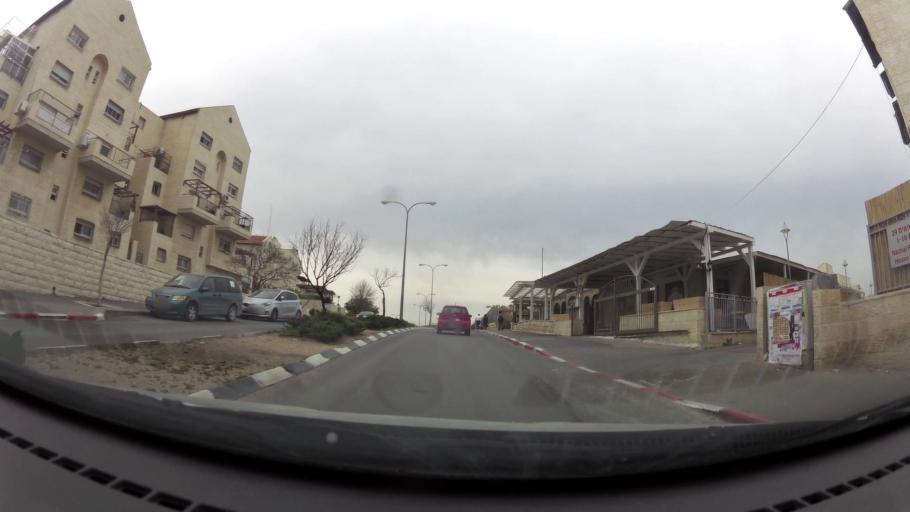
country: IL
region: Jerusalem
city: Bet Shemesh
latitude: 31.7096
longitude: 34.9975
